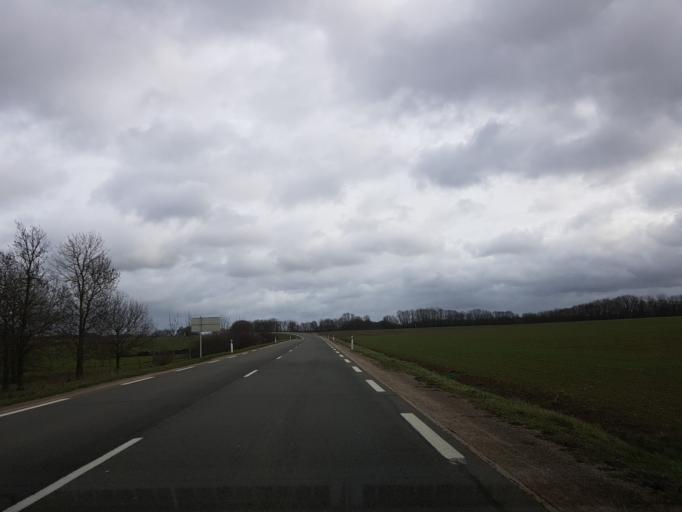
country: FR
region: Champagne-Ardenne
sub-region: Departement de la Haute-Marne
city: Chalindrey
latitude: 47.8446
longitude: 5.4506
